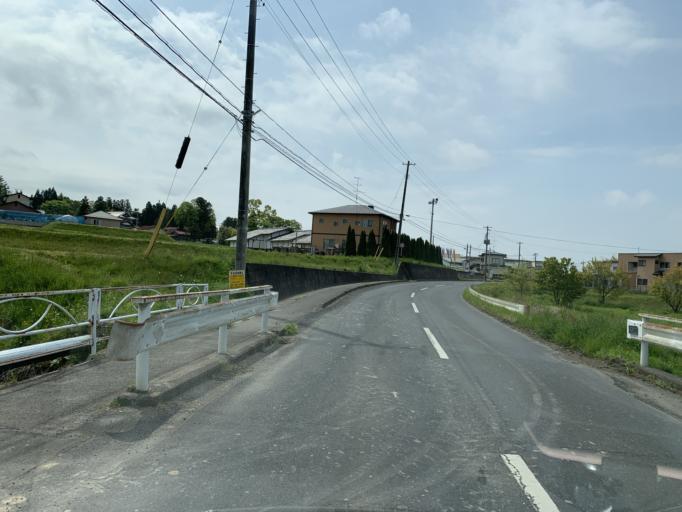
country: JP
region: Iwate
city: Ichinoseki
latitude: 38.8295
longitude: 141.2020
